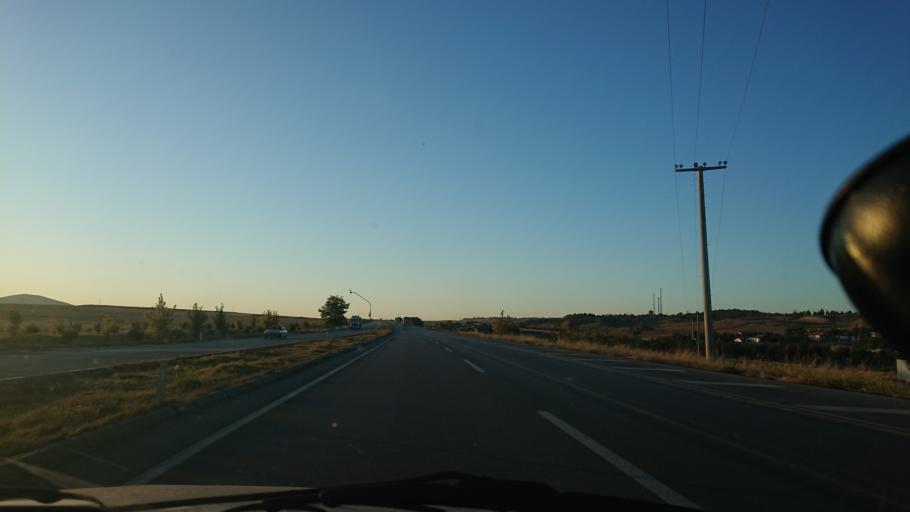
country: TR
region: Eskisehir
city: Mahmudiye
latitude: 39.4896
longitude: 30.9793
